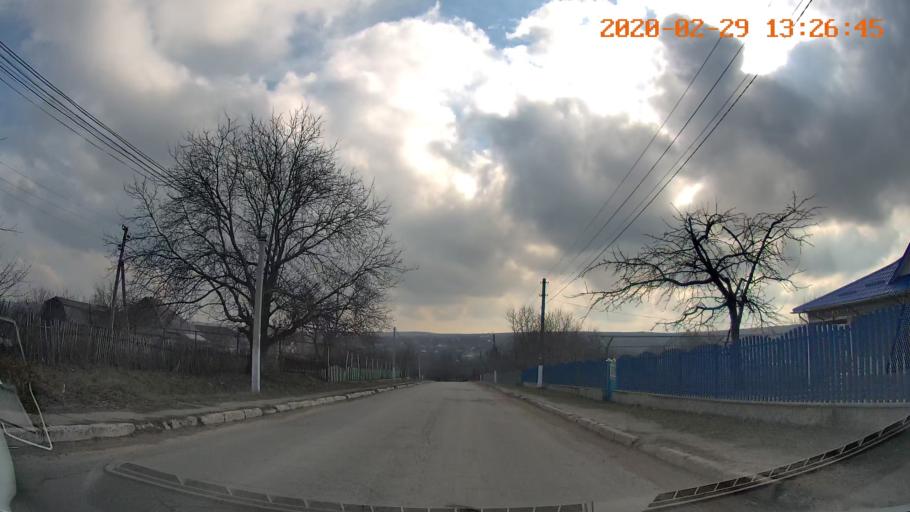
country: MD
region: Telenesti
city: Camenca
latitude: 47.9175
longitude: 28.6389
